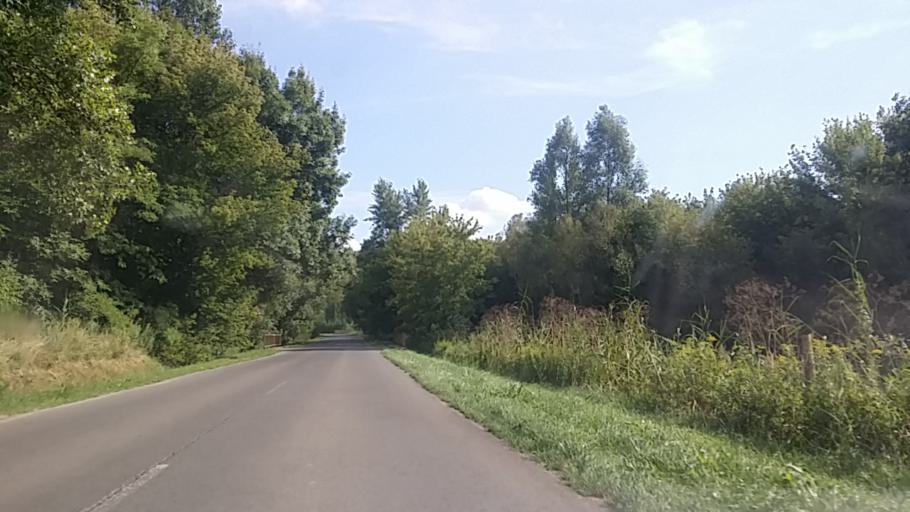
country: HU
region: Tolna
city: Gyonk
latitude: 46.5322
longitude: 18.5047
